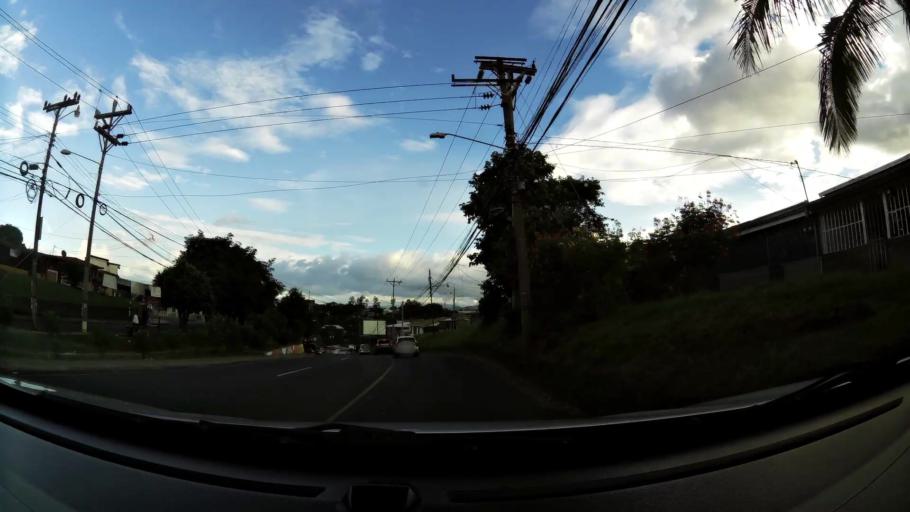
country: CR
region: Alajuela
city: Alajuela
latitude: 10.0052
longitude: -84.2048
